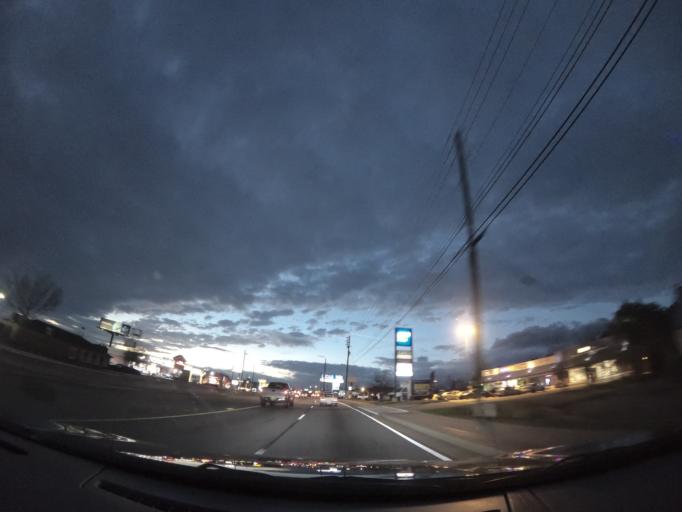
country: US
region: Georgia
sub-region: Cherokee County
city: Woodstock
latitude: 34.0876
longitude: -84.5741
